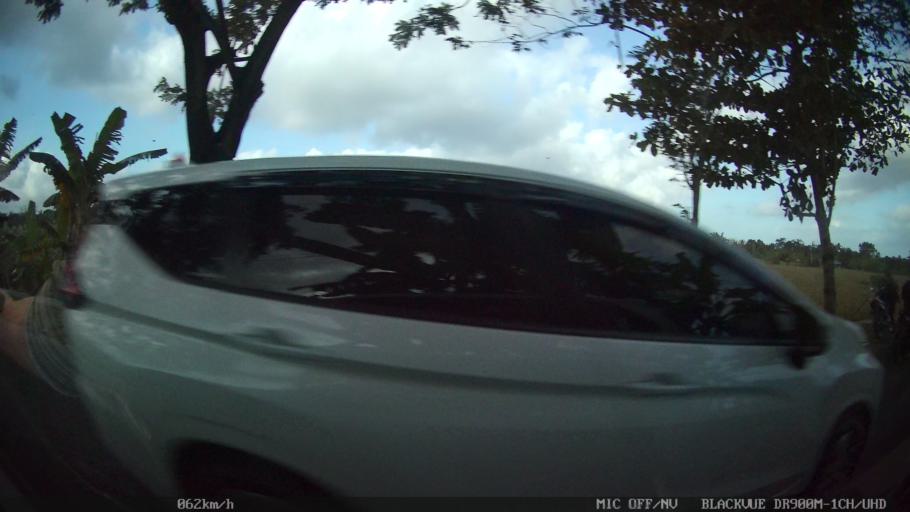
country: ID
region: Bali
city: Banjar Mambalkajanan
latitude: -8.5563
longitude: 115.2325
